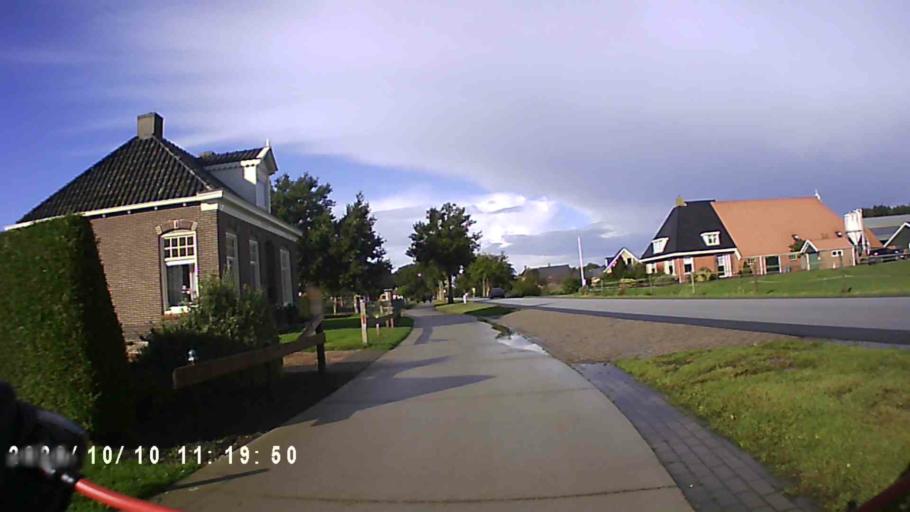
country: NL
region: Friesland
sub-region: Gemeente Smallingerland
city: Drachtstercompagnie
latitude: 53.0950
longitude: 6.1893
